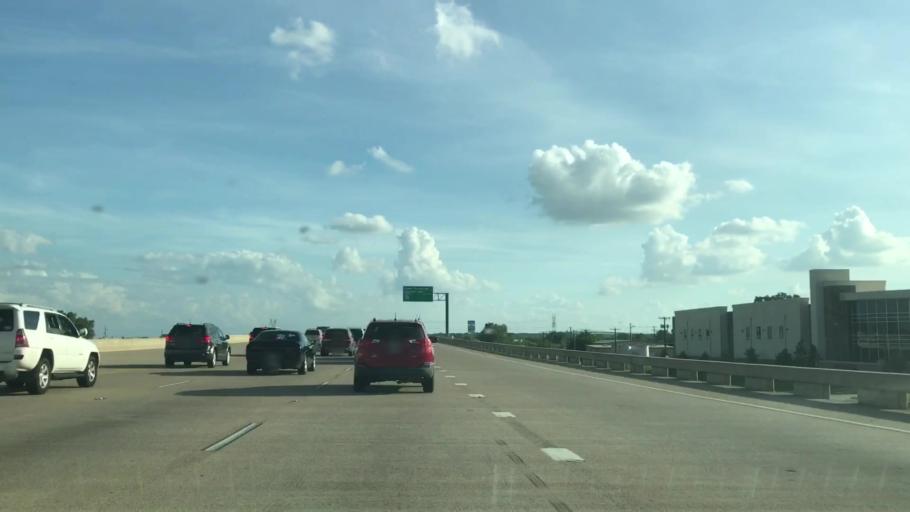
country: US
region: Texas
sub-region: Dallas County
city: Grand Prairie
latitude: 32.7956
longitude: -97.0185
